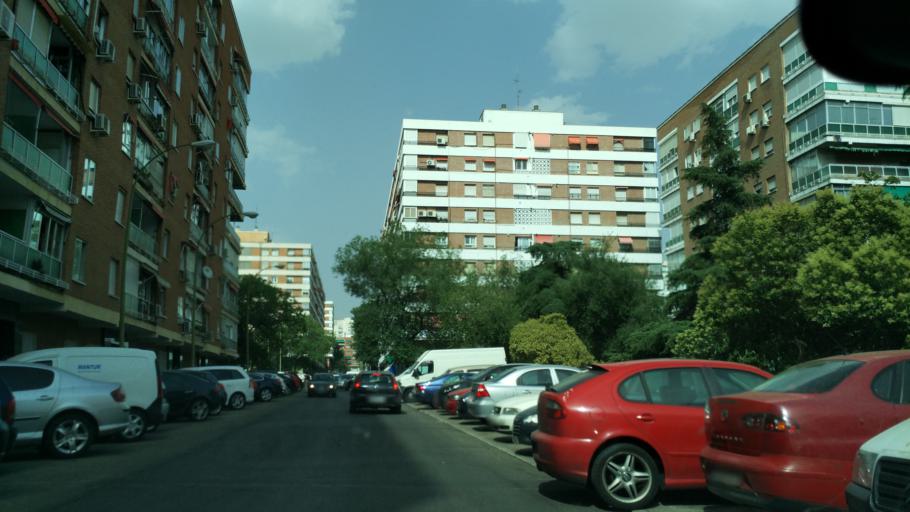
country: ES
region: Madrid
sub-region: Provincia de Madrid
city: Tetuan de las Victorias
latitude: 40.4797
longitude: -3.7210
